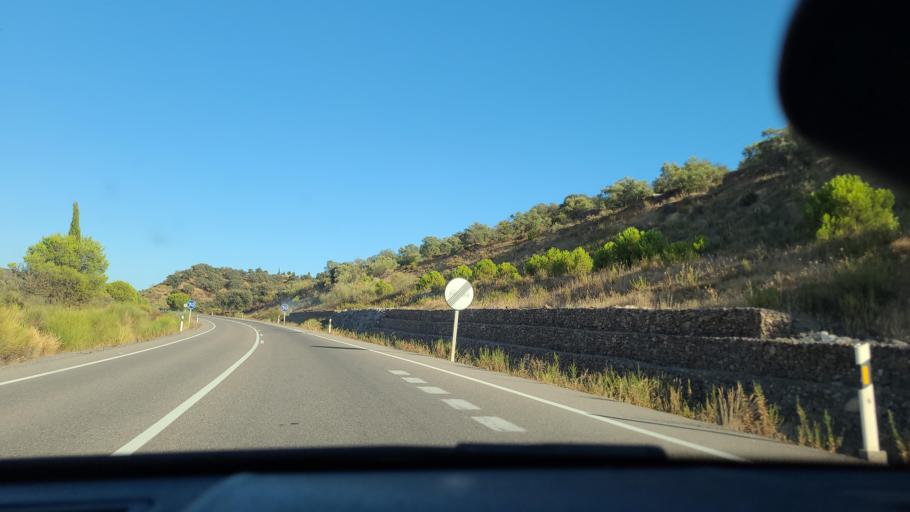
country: ES
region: Andalusia
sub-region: Province of Cordoba
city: Espiel
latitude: 38.1756
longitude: -5.0134
